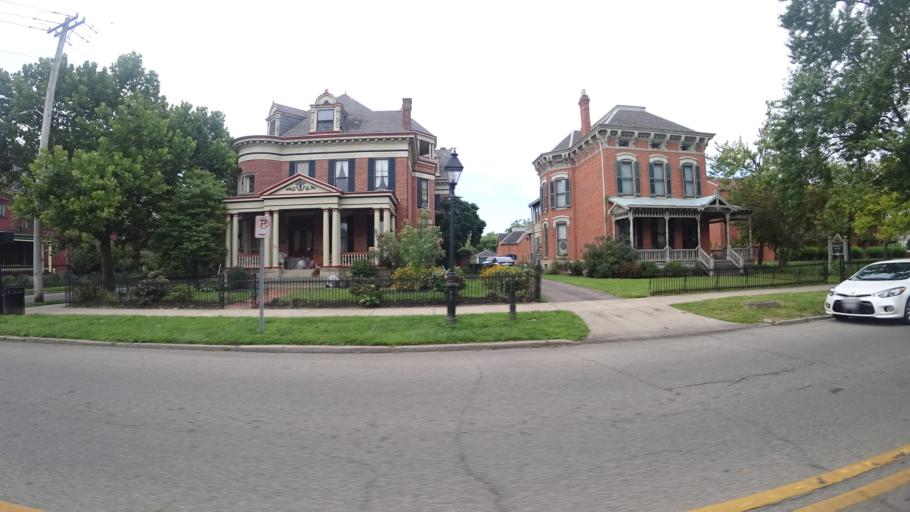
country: US
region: Ohio
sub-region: Butler County
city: Hamilton
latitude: 39.4001
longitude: -84.5536
